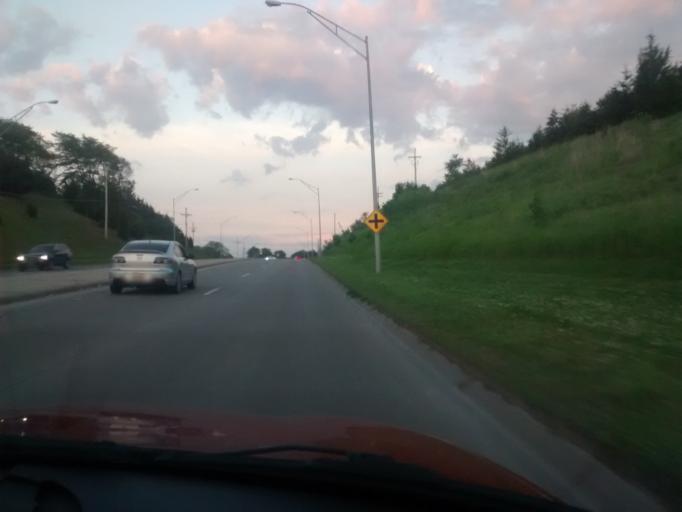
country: US
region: Nebraska
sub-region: Sarpy County
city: Offutt Air Force Base
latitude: 41.1607
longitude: -95.9588
